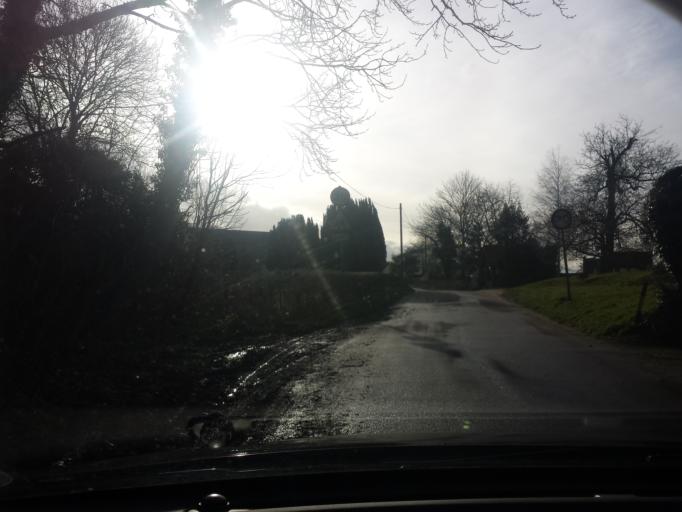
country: GB
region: England
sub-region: Essex
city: Alresford
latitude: 51.8963
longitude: 1.0278
